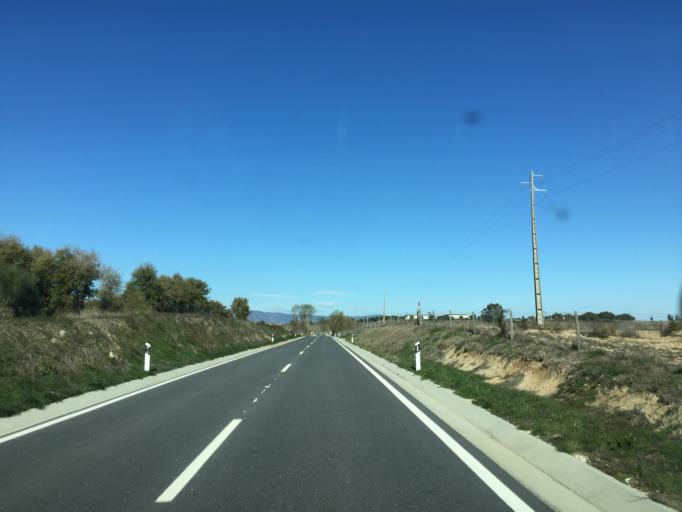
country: PT
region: Guarda
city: Alcains
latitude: 39.9613
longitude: -7.4539
